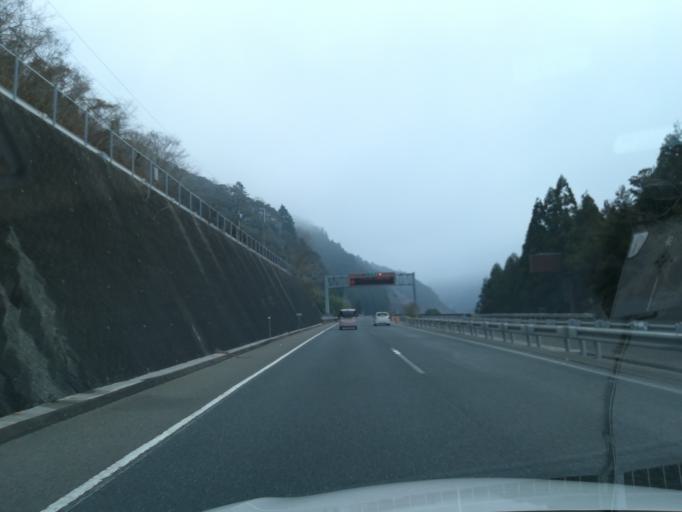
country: JP
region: Ehime
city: Kawanoecho
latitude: 33.7798
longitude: 133.6610
